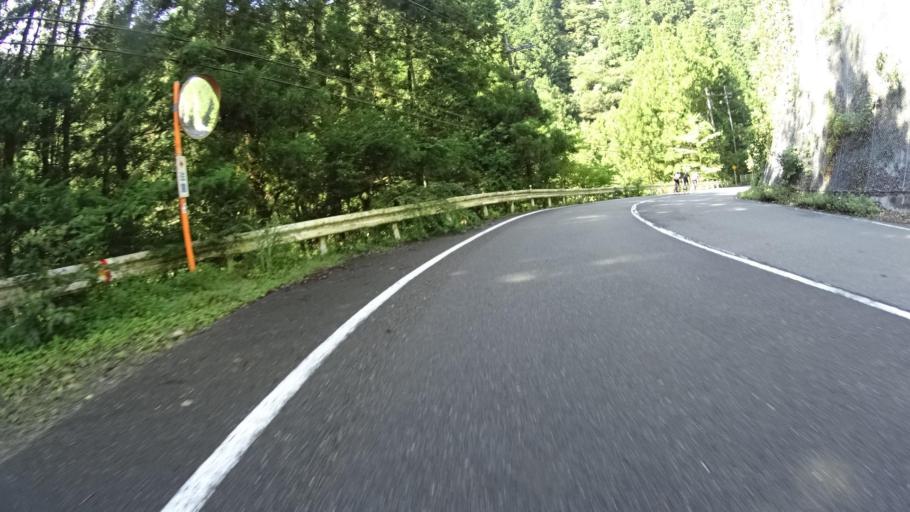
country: JP
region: Yamanashi
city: Uenohara
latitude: 35.7385
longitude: 139.0867
